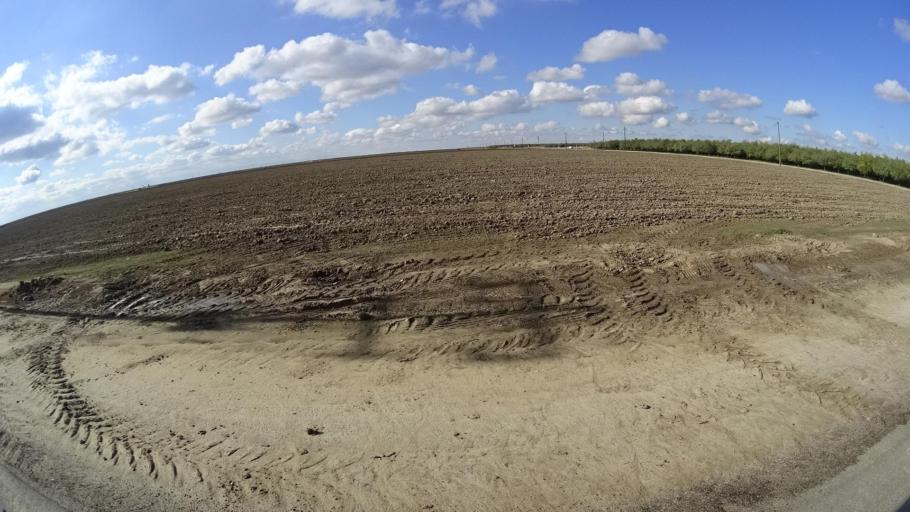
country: US
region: California
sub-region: Kern County
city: McFarland
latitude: 35.6735
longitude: -119.2586
